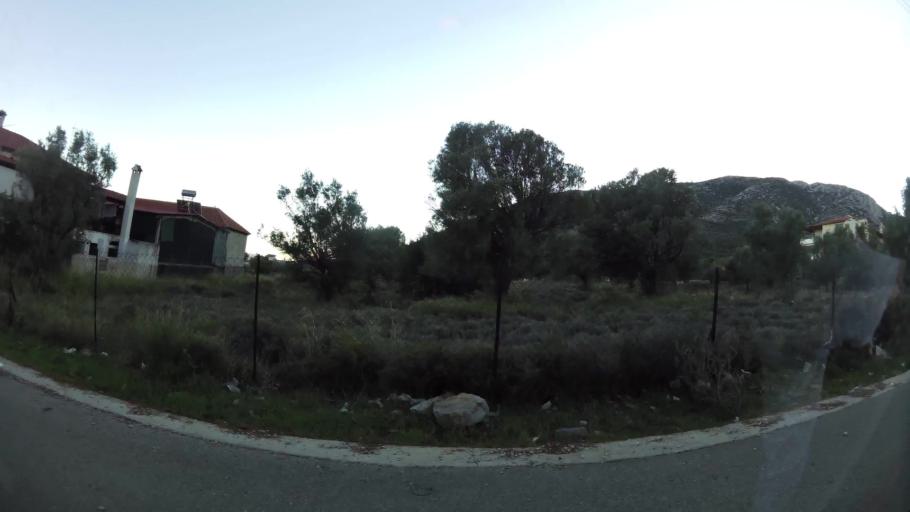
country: GR
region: Attica
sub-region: Nomarchia Anatolikis Attikis
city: Leondarion
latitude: 37.9717
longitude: 23.8386
